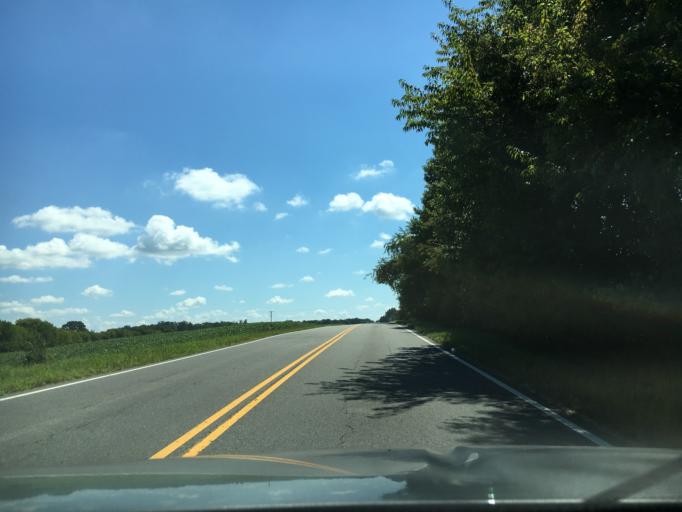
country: US
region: Virginia
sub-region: Amelia County
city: Amelia Court House
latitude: 37.3898
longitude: -77.8990
